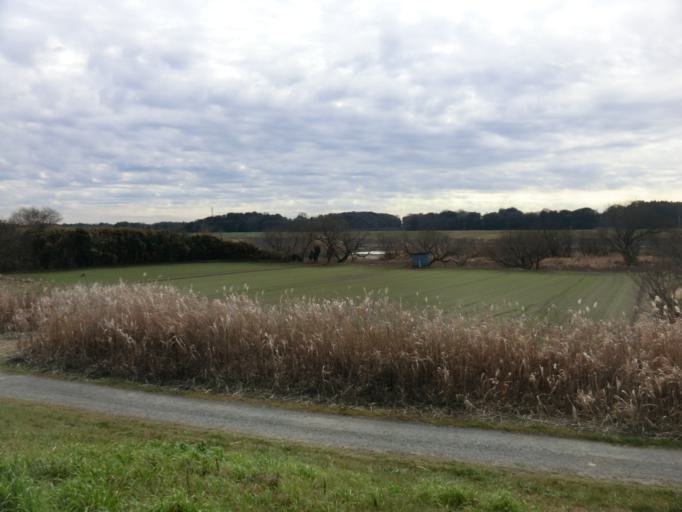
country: JP
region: Ibaraki
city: Moriya
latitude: 35.9388
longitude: 140.0390
